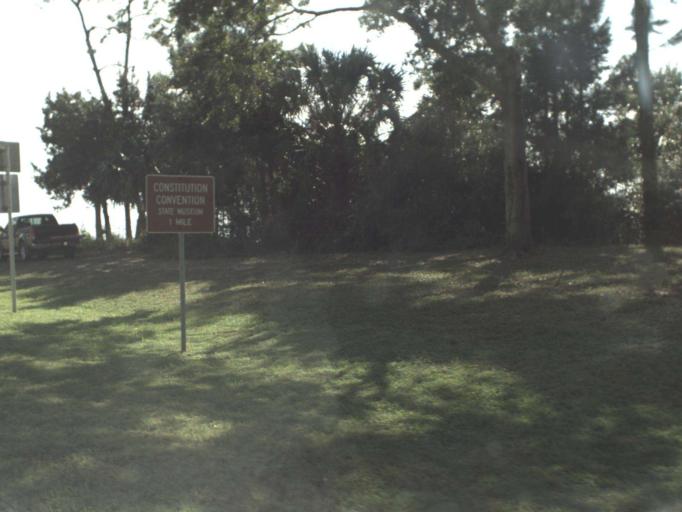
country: US
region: Florida
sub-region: Gulf County
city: Port Saint Joe
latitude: 29.8070
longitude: -85.3019
